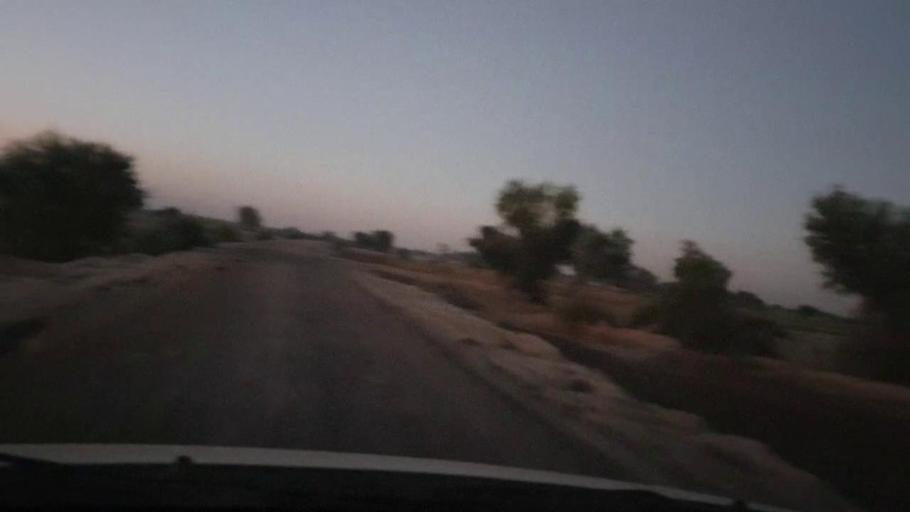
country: PK
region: Sindh
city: Phulji
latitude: 26.9018
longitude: 67.4713
